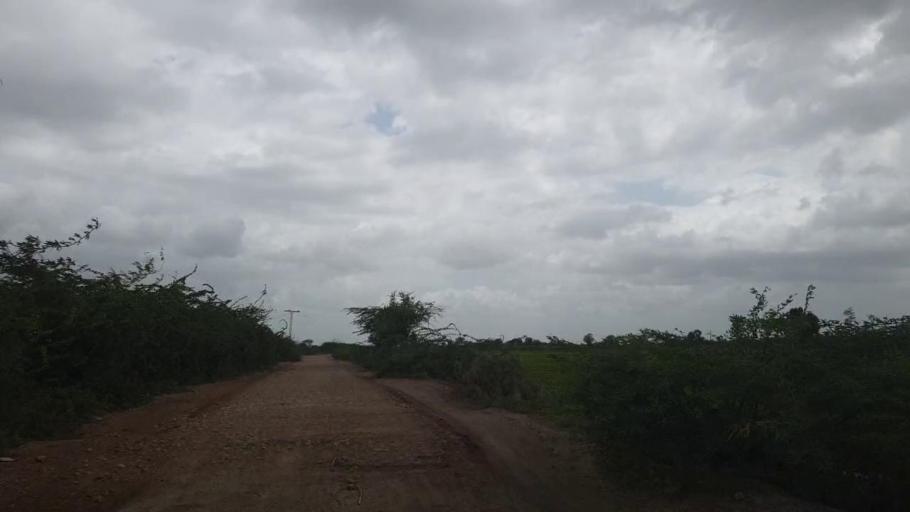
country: PK
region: Sindh
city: Badin
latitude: 24.6527
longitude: 68.9459
